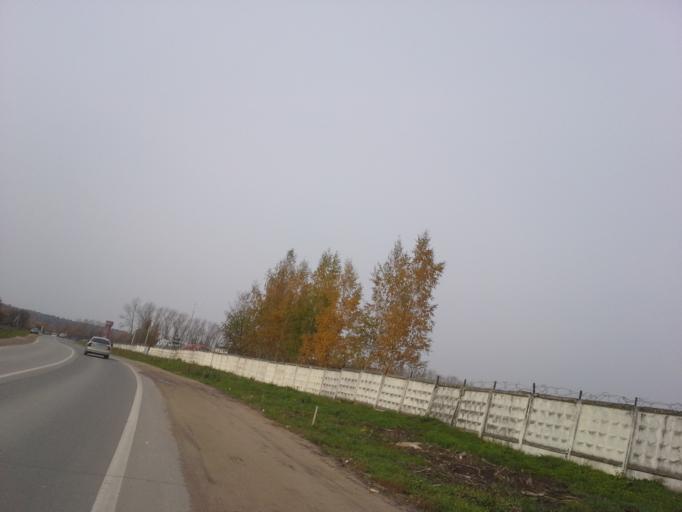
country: RU
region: Moskovskaya
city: Bol'shiye Vyazemy
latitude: 55.6372
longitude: 37.0032
